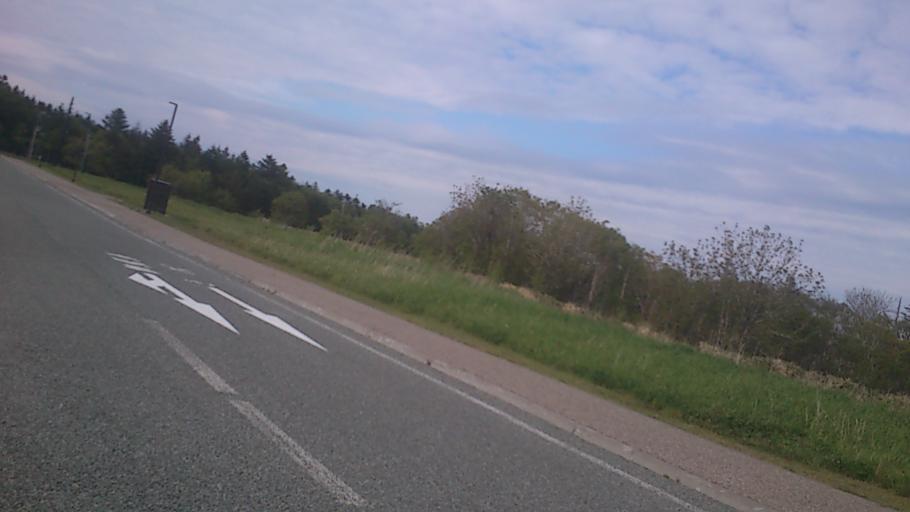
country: JP
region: Hokkaido
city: Makubetsu
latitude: 45.1114
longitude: 141.7040
